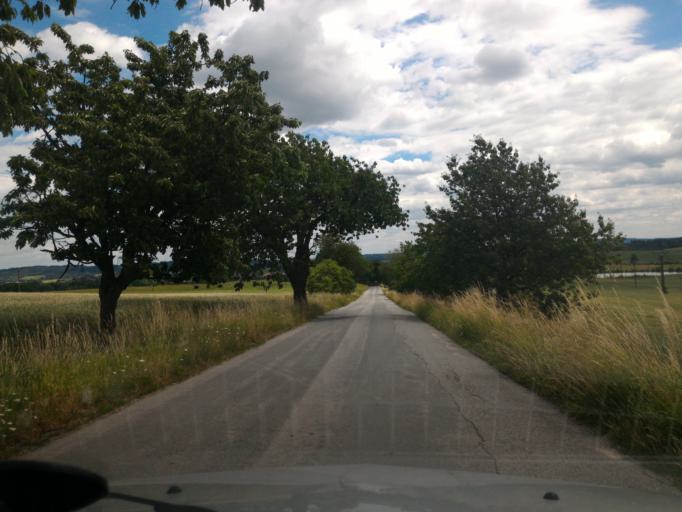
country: CZ
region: Vysocina
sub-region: Okres Jihlava
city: Telc
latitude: 49.1882
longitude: 15.4230
